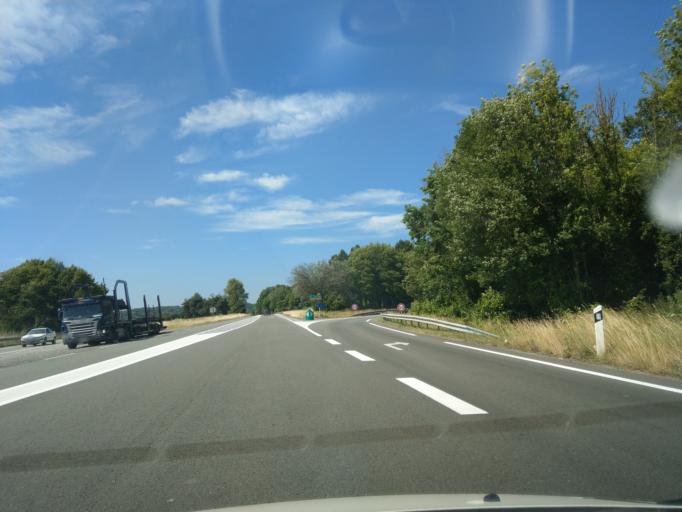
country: FR
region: Franche-Comte
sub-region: Territoire de Belfort
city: Offemont
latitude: 47.6618
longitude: 6.9074
